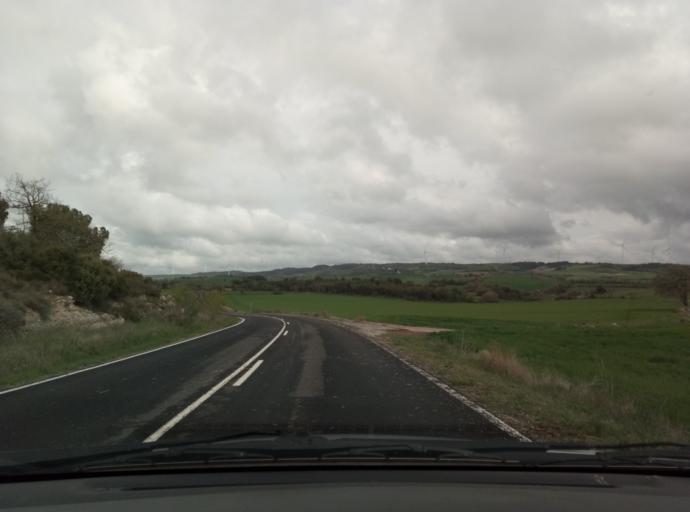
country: ES
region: Catalonia
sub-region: Provincia de Tarragona
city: Santa Coloma de Queralt
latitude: 41.5724
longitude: 1.3401
